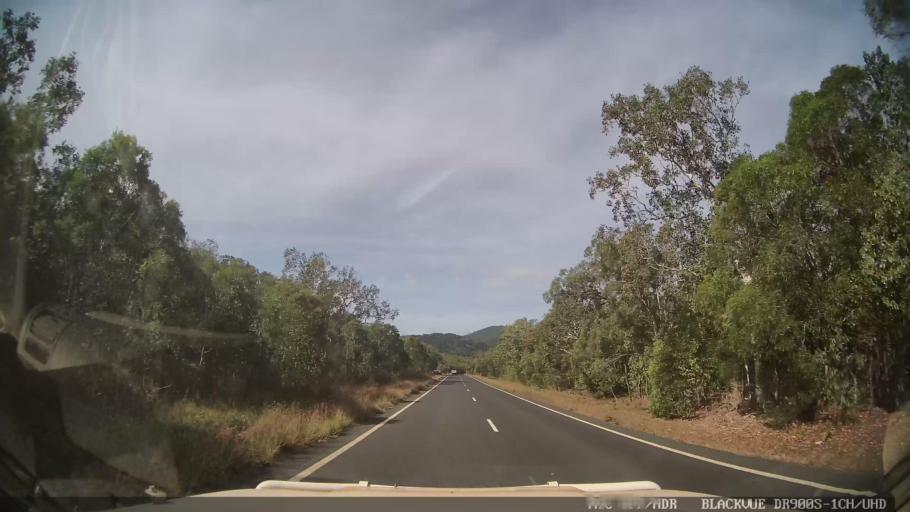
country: AU
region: Queensland
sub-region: Cook
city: Cooktown
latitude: -15.5042
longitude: 145.2348
